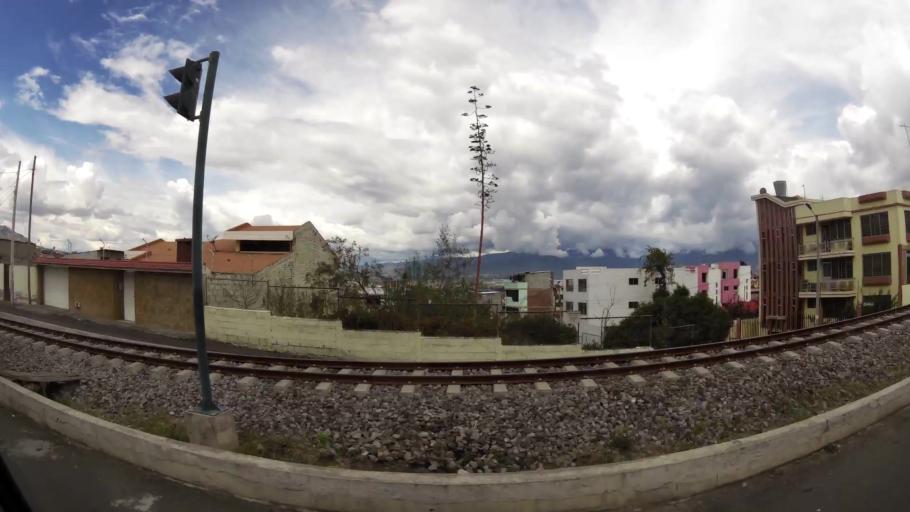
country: EC
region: Tungurahua
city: Ambato
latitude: -1.2515
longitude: -78.6193
